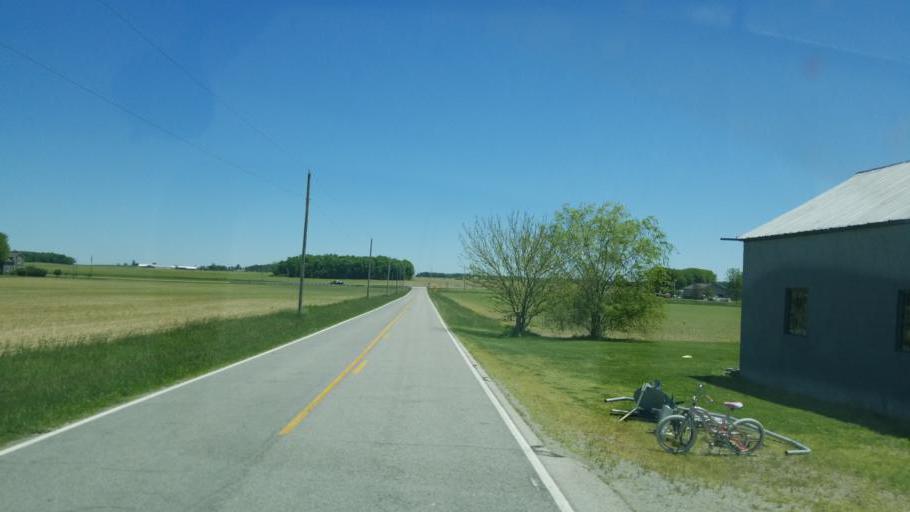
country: US
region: Ohio
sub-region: Darke County
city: Ansonia
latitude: 40.2795
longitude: -84.7133
